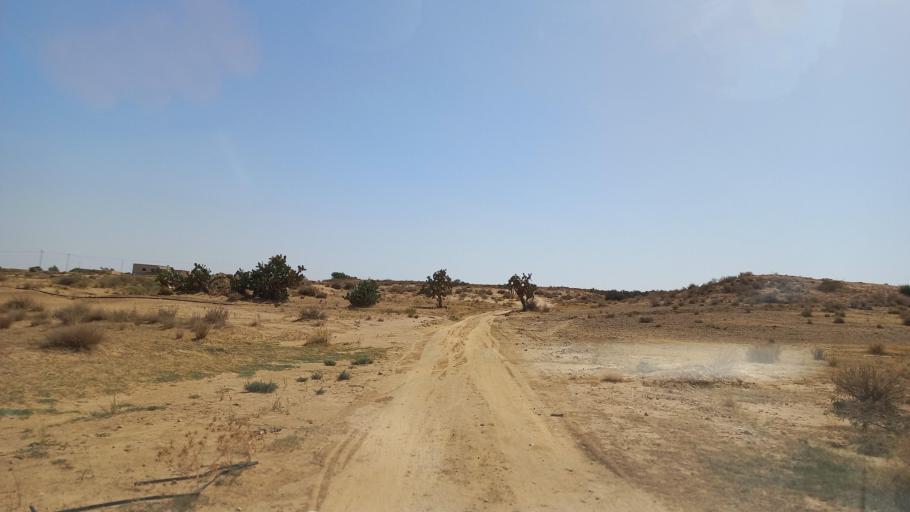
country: TN
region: Al Qasrayn
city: Kasserine
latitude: 35.2216
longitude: 9.0358
